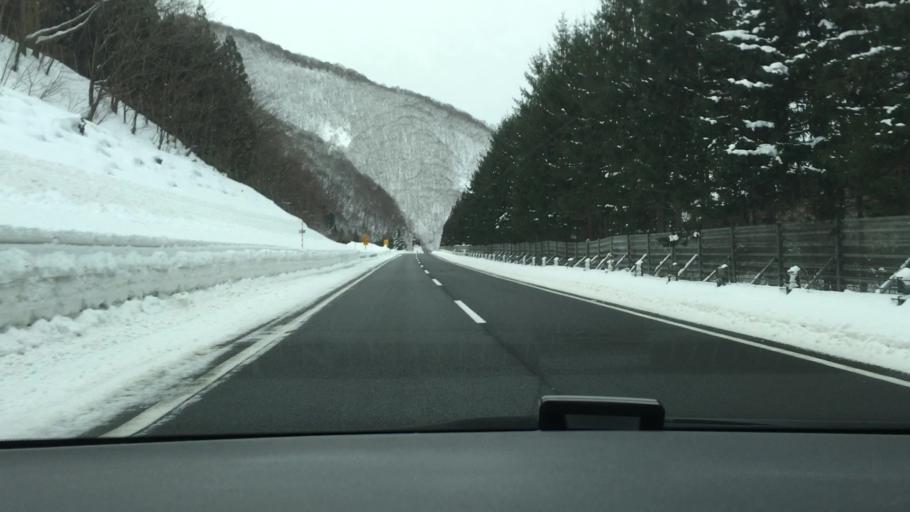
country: JP
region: Akita
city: Hanawa
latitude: 40.1146
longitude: 140.8751
